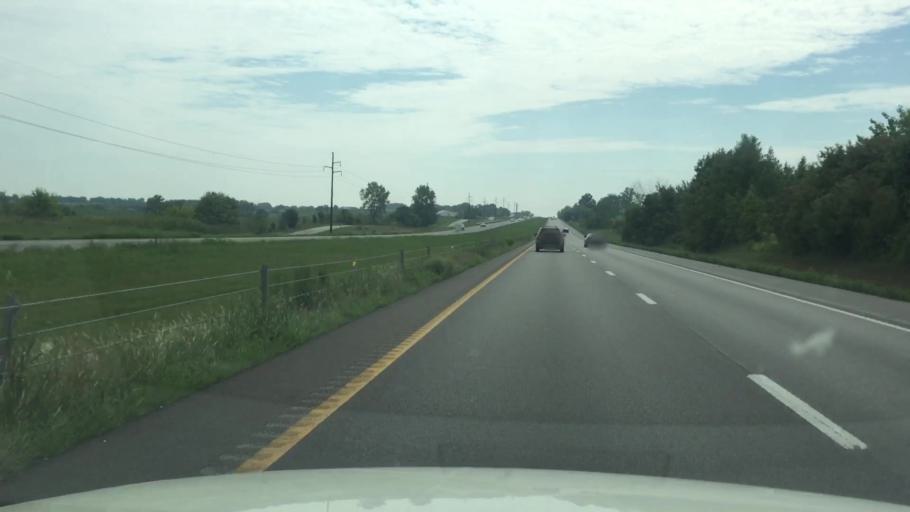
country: US
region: Missouri
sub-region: Clay County
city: Kearney
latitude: 39.3138
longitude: -94.4015
